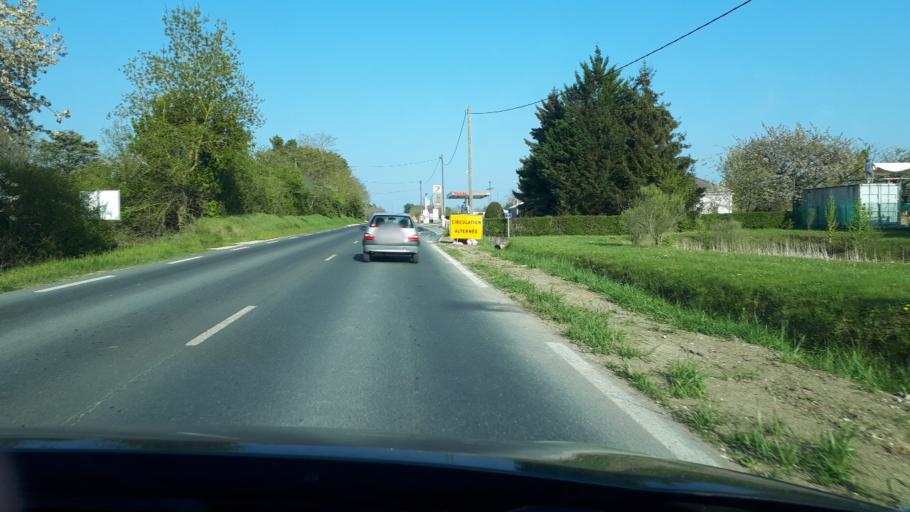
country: FR
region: Centre
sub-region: Departement du Loir-et-Cher
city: Saint-Georges-sur-Cher
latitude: 47.3299
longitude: 1.1482
